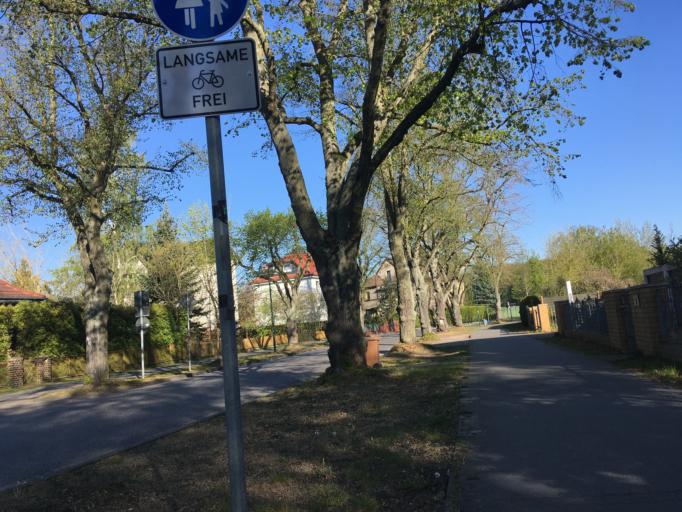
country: DE
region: Berlin
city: Buch
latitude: 52.6604
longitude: 13.5312
